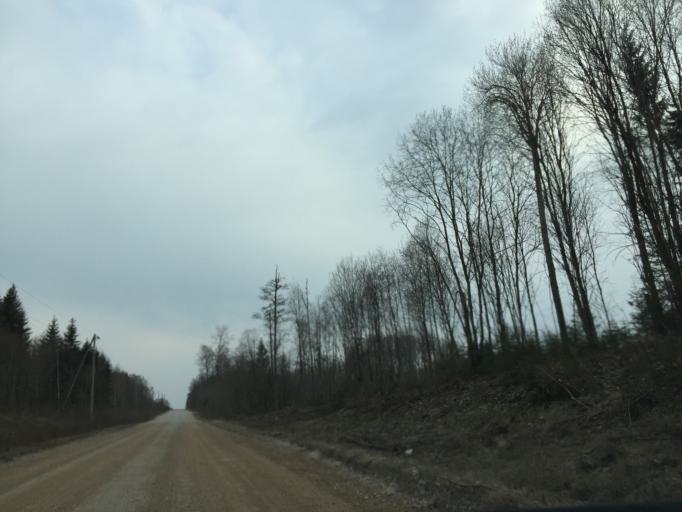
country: LV
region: Priekuli
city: Priekuli
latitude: 57.1837
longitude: 25.4671
